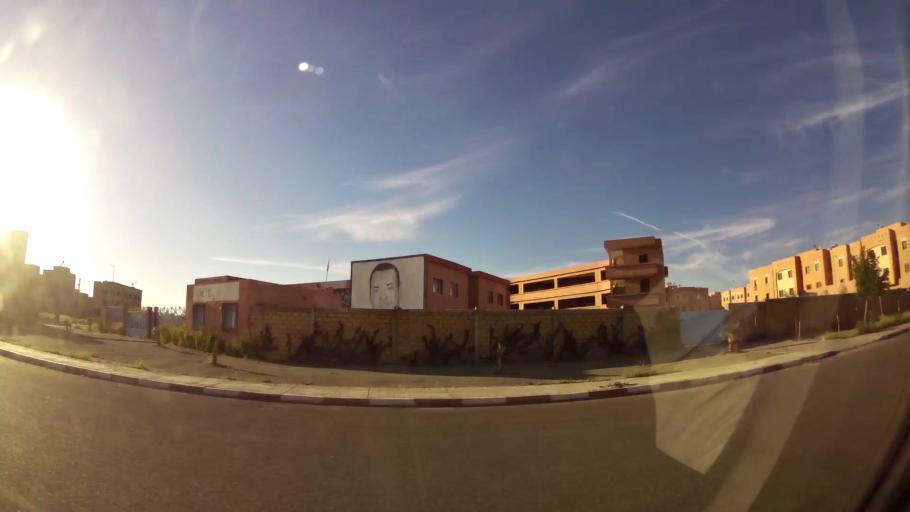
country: MA
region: Marrakech-Tensift-Al Haouz
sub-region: Marrakech
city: Marrakesh
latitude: 31.7621
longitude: -8.1114
